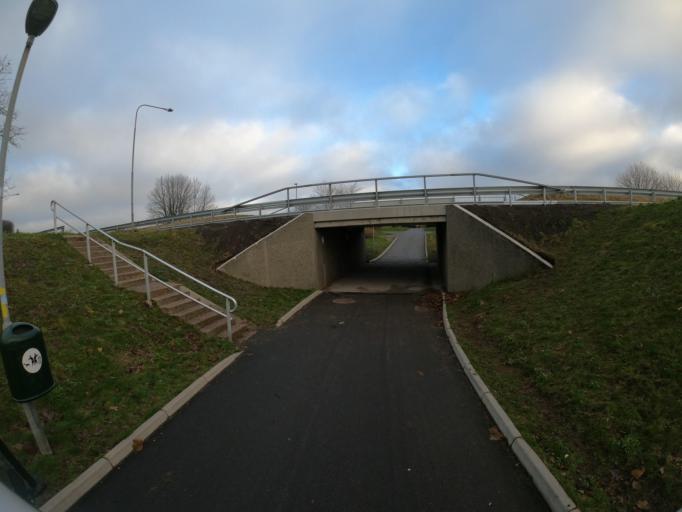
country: SE
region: Skane
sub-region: Svedala Kommun
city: Svedala
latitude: 55.5156
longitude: 13.2220
